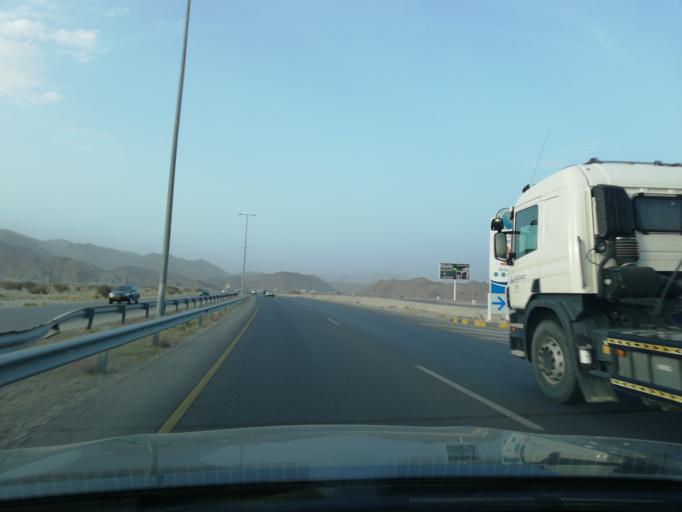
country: OM
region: Muhafazat ad Dakhiliyah
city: Bidbid
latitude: 23.3839
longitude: 58.0574
